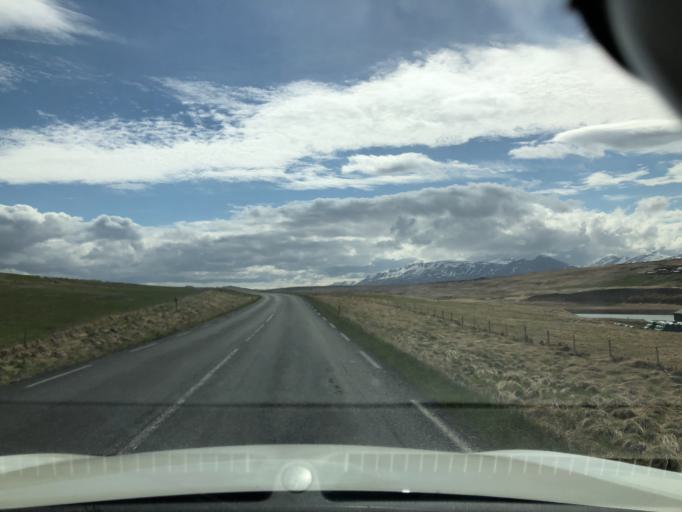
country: IS
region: Northwest
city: Saudarkrokur
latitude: 65.6356
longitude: -20.1589
